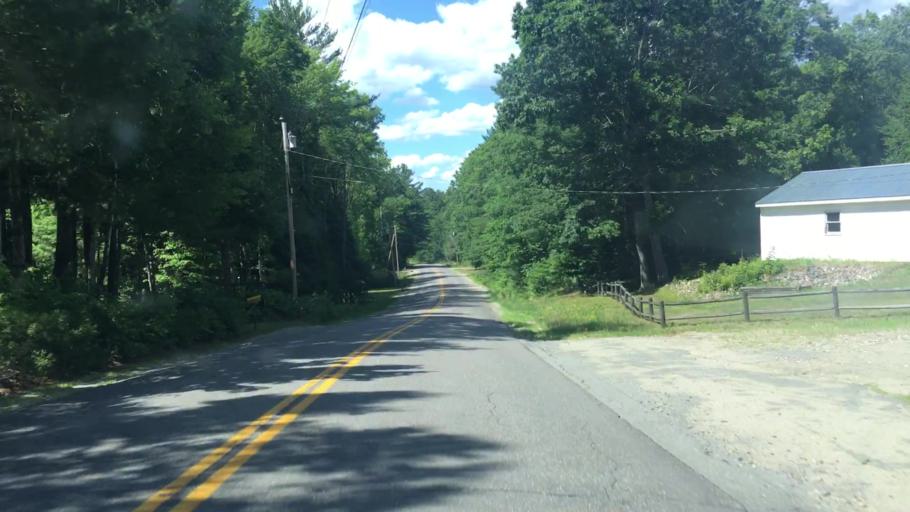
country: US
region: Maine
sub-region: Franklin County
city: Chesterville
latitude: 44.5644
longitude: -70.0864
